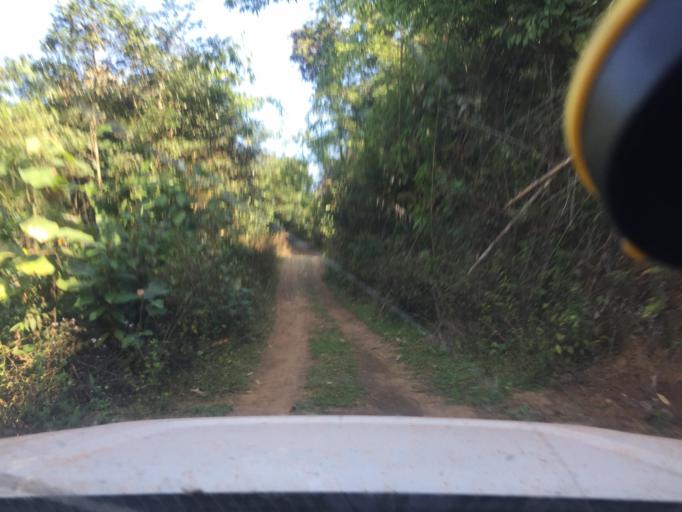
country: LA
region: Phongsali
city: Phongsali
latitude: 21.7035
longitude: 102.3945
